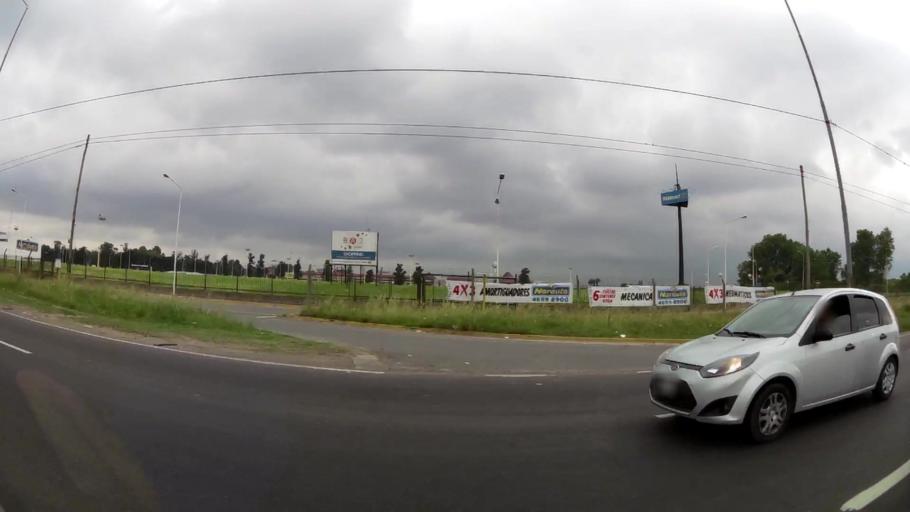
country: AR
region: Buenos Aires
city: San Justo
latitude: -34.7040
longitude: -58.5361
